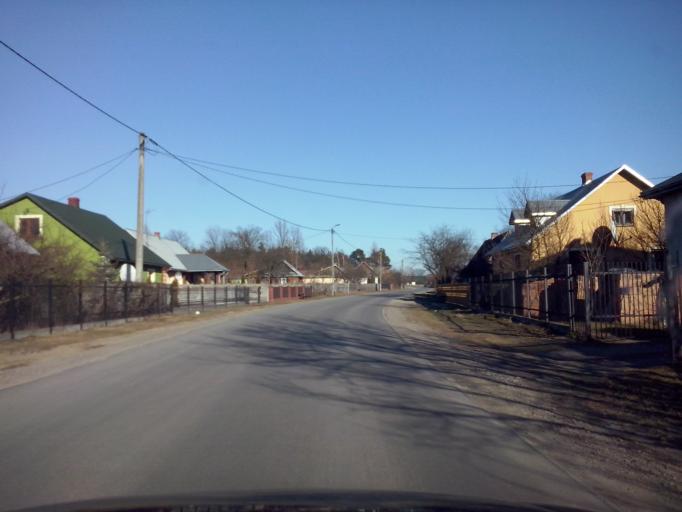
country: PL
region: Subcarpathian Voivodeship
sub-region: Powiat nizanski
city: Harasiuki
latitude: 50.5336
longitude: 22.4561
